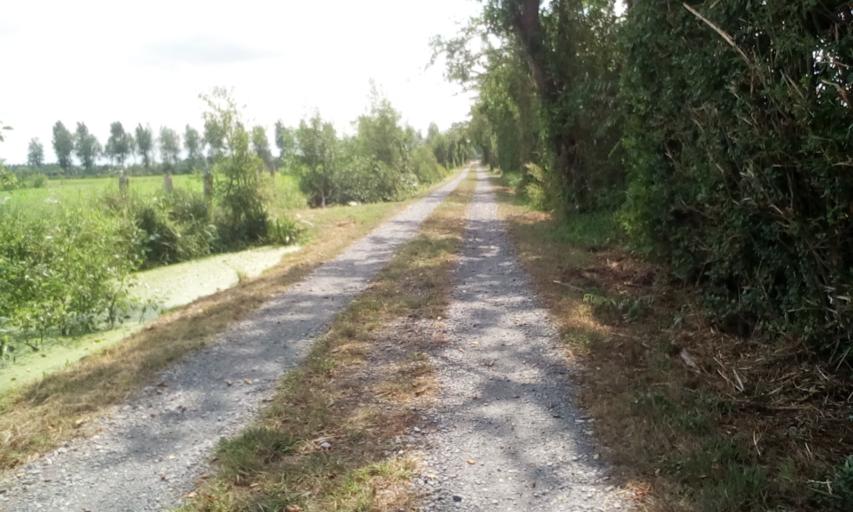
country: FR
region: Lower Normandy
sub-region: Departement du Calvados
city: Bavent
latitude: 49.2293
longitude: -0.1703
